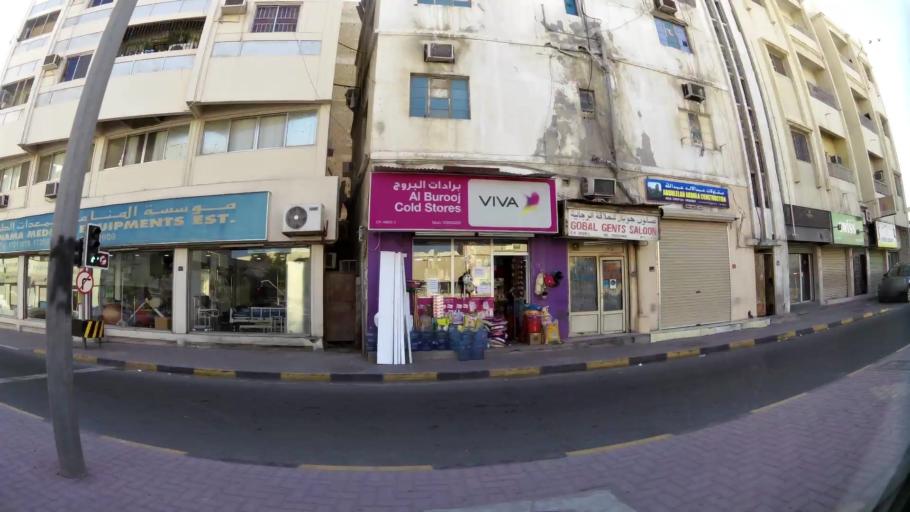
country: BH
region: Manama
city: Manama
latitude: 26.2349
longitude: 50.5831
